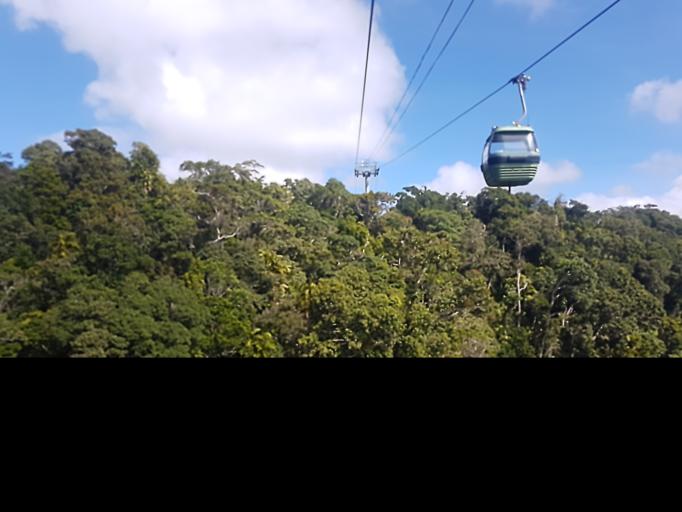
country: AU
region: Queensland
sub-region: Cairns
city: Redlynch
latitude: -16.8492
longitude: 145.6719
